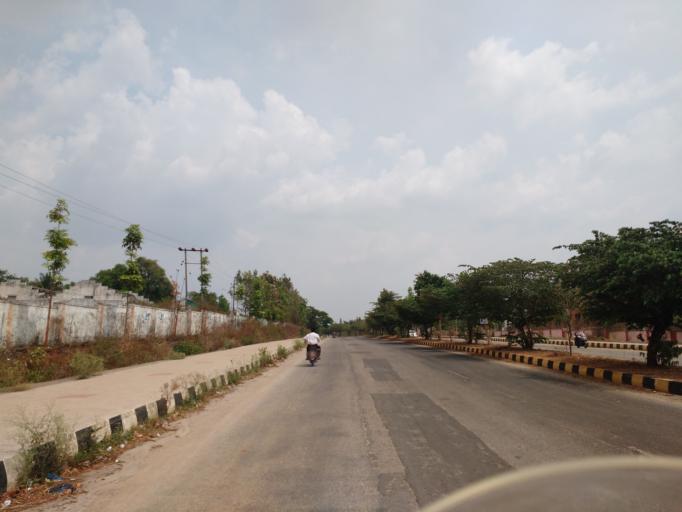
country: IN
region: Karnataka
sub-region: Hassan
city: Hassan
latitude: 13.0119
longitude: 76.1207
